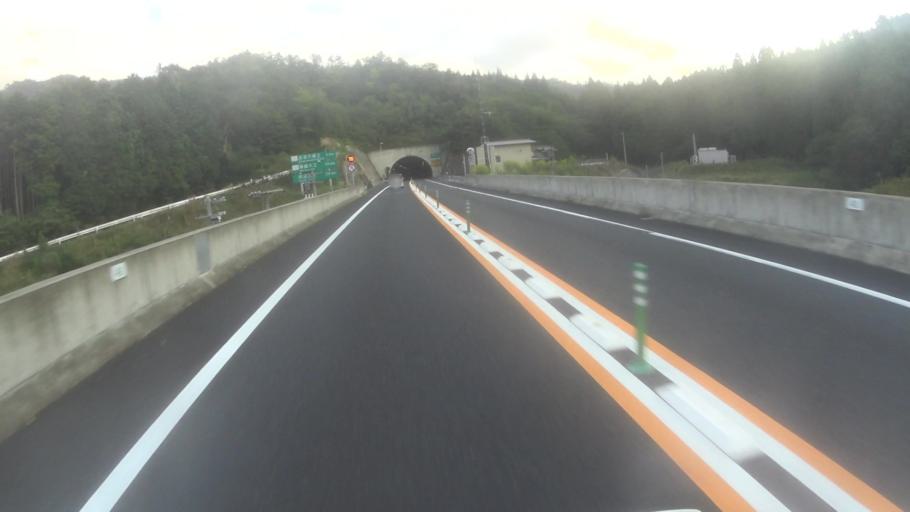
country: JP
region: Kyoto
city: Miyazu
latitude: 35.5425
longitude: 135.1556
